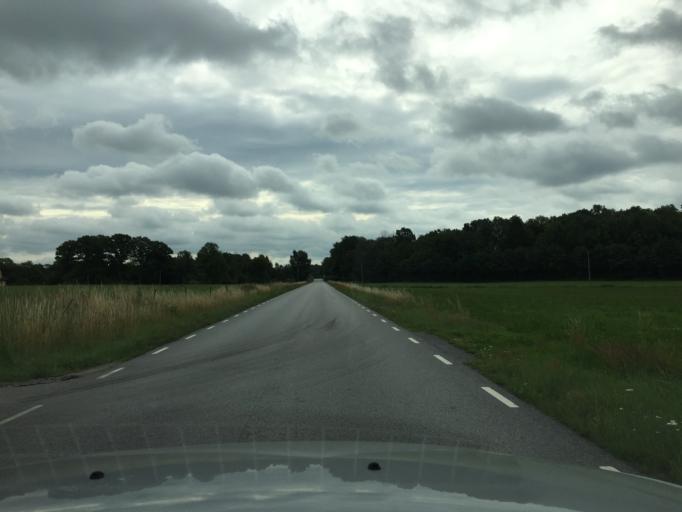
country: SE
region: Skane
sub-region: Hassleholms Kommun
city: Sosdala
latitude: 56.0461
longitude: 13.6602
